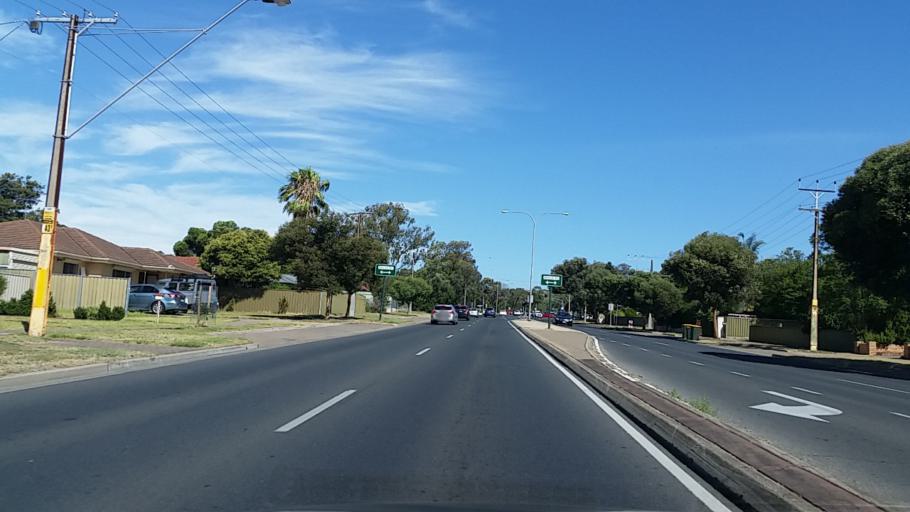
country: AU
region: South Australia
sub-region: Salisbury
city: Salisbury
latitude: -34.7966
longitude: 138.6551
